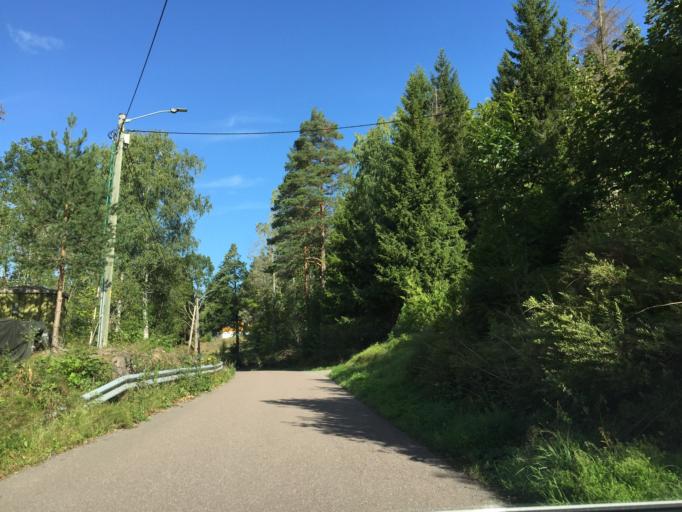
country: NO
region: Vestfold
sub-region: Holmestrand
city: Gullhaug
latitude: 59.4780
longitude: 10.1786
